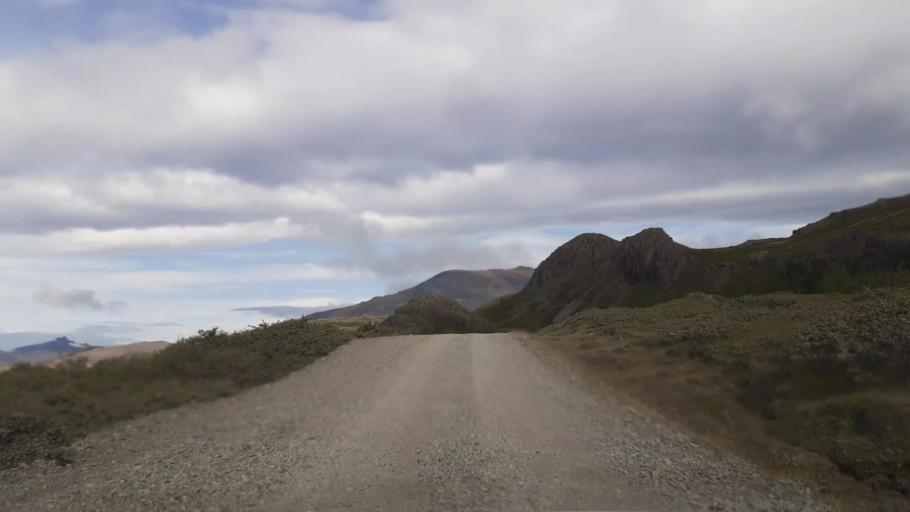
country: IS
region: East
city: Hoefn
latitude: 64.4285
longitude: -14.8856
